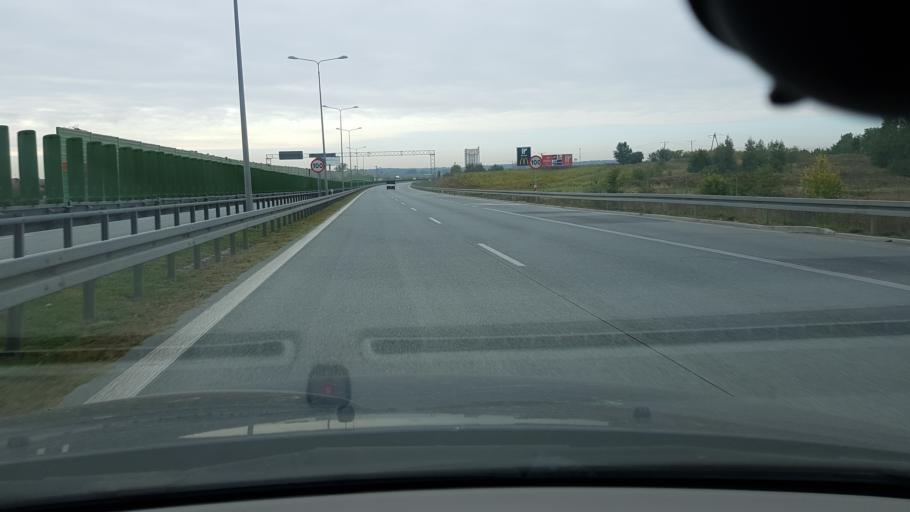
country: PL
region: Lodz Voivodeship
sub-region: Powiat rawski
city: Rawa Mazowiecka
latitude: 51.7718
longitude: 20.2736
